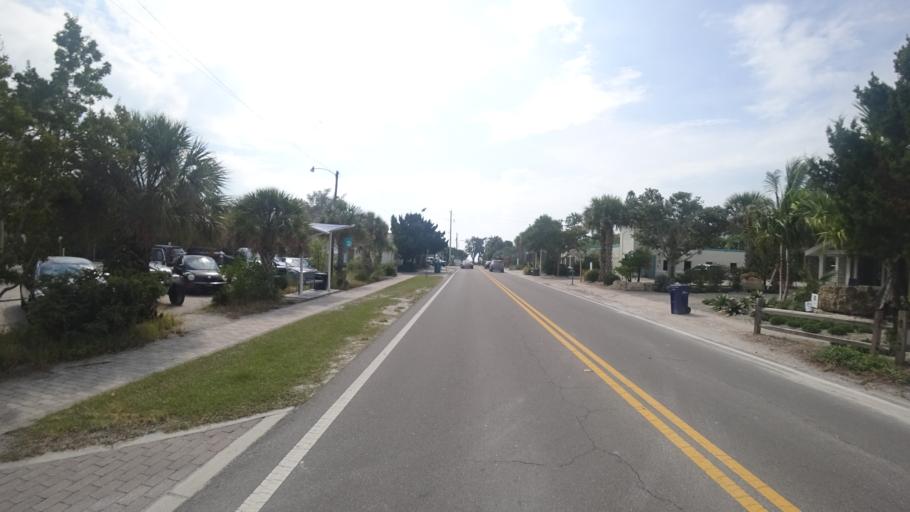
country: US
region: Florida
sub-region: Manatee County
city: Anna Maria
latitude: 27.5275
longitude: -82.7363
